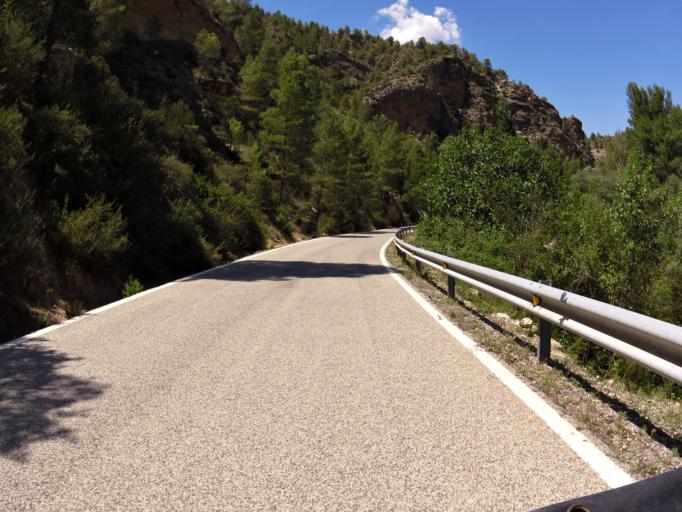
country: ES
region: Valencia
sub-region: Provincia de Valencia
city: Casas Bajas
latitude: 39.9934
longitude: -1.2782
